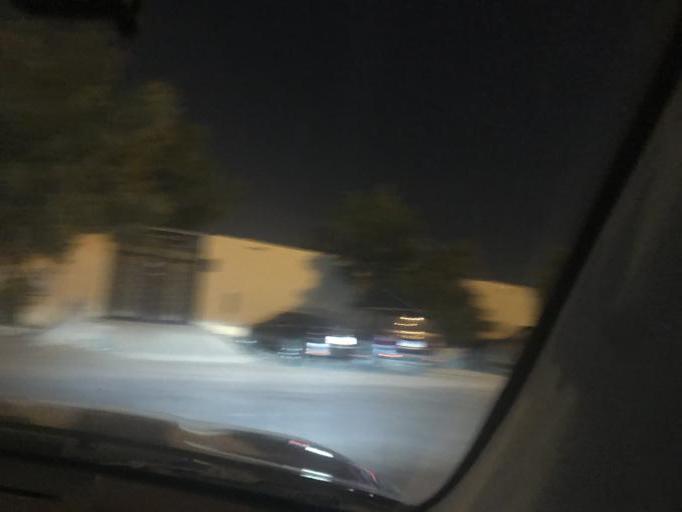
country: SA
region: Ar Riyad
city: Riyadh
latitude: 24.8244
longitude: 46.7400
